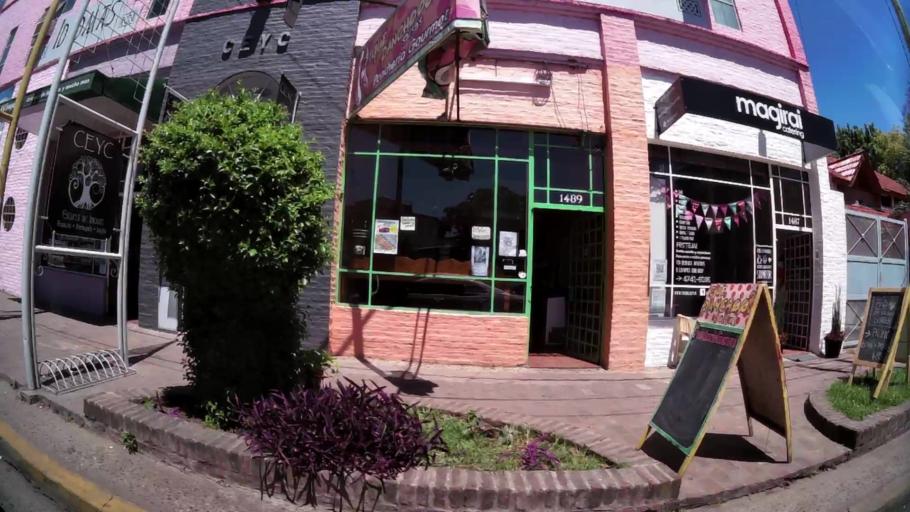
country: AR
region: Buenos Aires
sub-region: Partido de Tigre
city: Tigre
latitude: -34.4941
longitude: -58.6320
